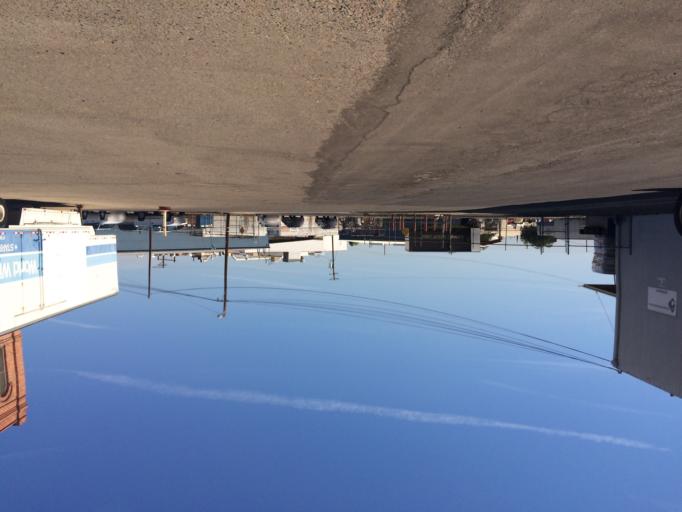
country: US
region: California
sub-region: Fresno County
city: Fresno
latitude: 36.7269
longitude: -119.7767
